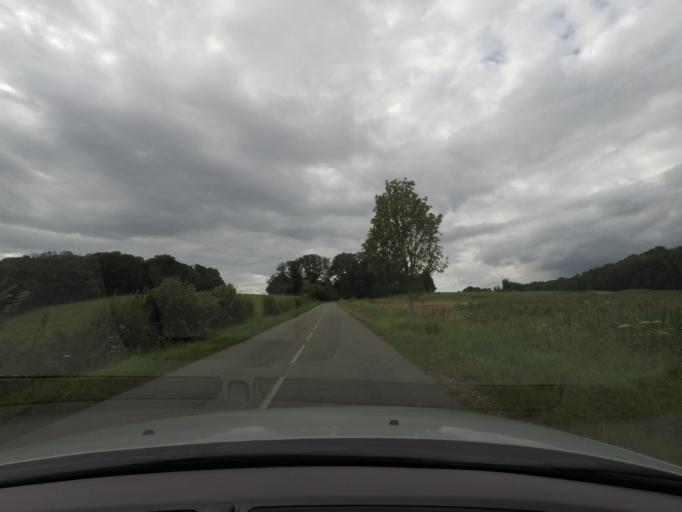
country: FR
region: Haute-Normandie
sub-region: Departement de l'Eure
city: Les Andelys
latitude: 49.2825
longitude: 1.3497
